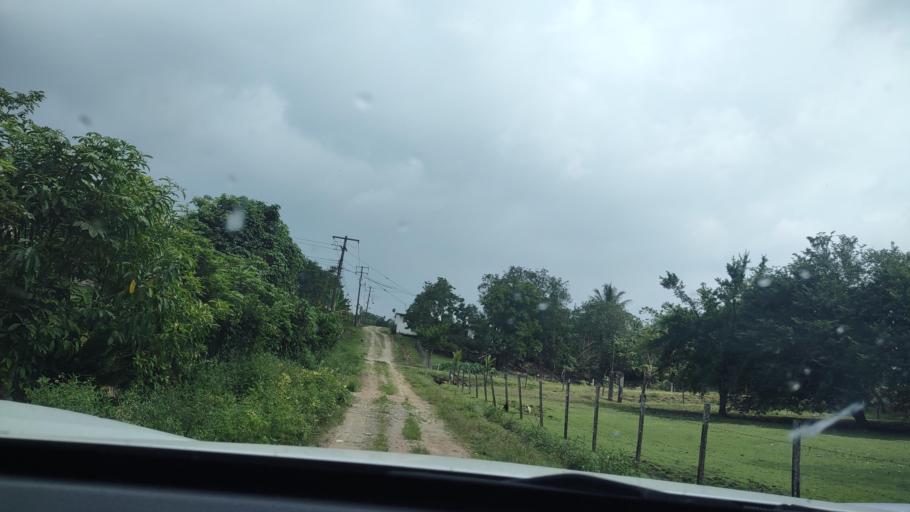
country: MX
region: Veracruz
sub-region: Uxpanapa
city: Poblado 10
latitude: 17.5491
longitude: -94.2948
